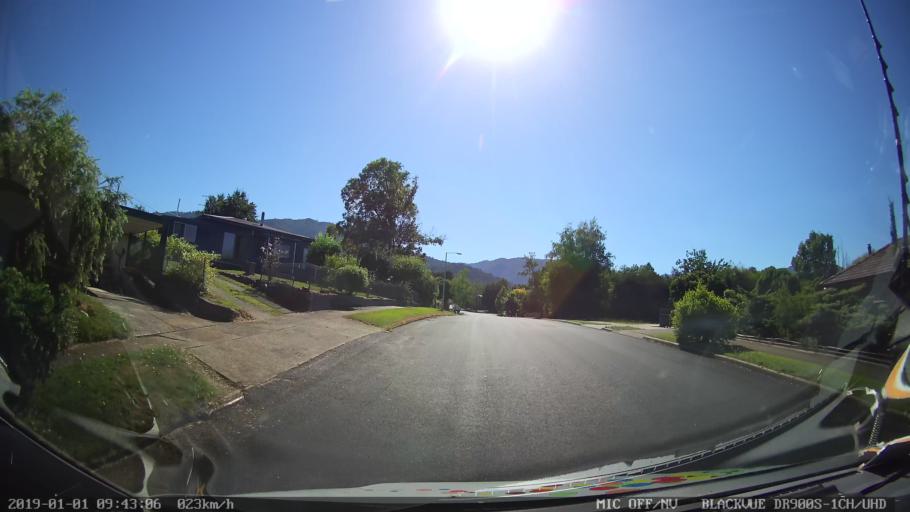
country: AU
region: New South Wales
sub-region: Snowy River
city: Jindabyne
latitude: -36.2156
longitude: 148.1326
